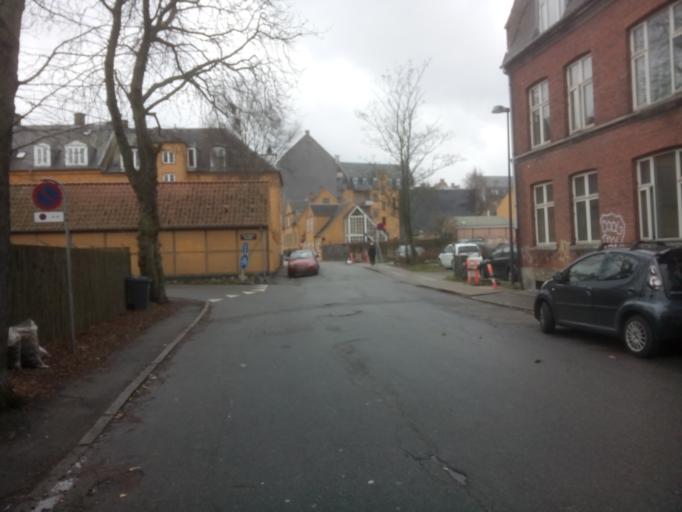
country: DK
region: Capital Region
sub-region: Frederiksberg Kommune
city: Frederiksberg
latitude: 55.6673
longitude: 12.5139
